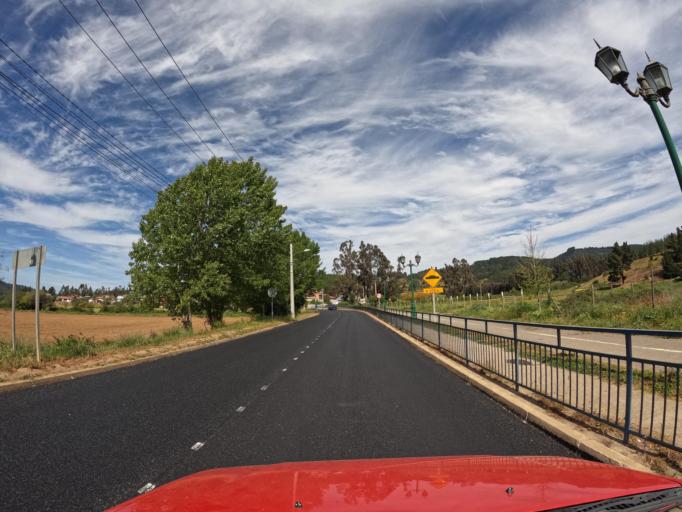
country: CL
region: Maule
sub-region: Provincia de Talca
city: Constitucion
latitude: -35.0977
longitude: -72.0153
